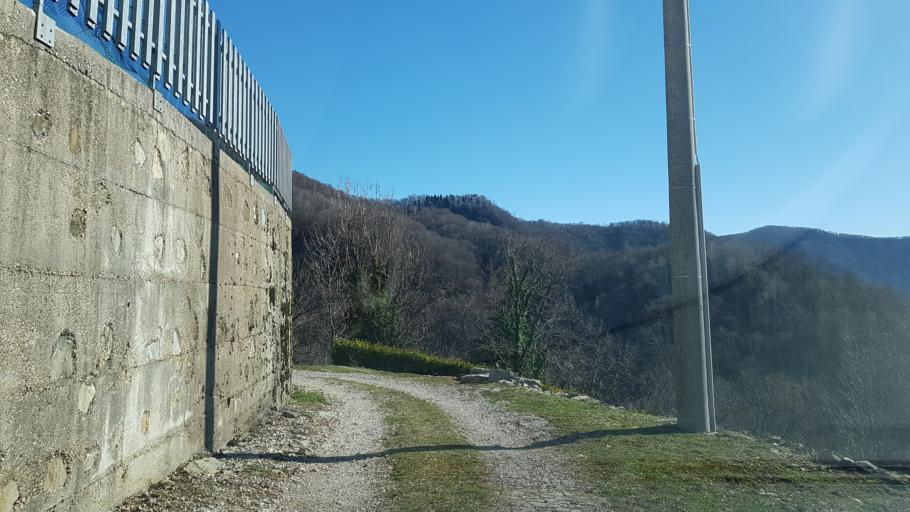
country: IT
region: Friuli Venezia Giulia
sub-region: Provincia di Udine
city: Taipana
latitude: 46.2339
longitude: 13.3037
